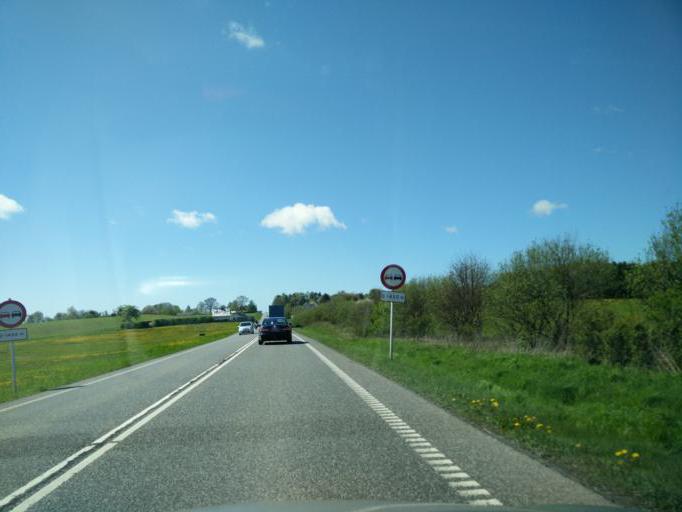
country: DK
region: Capital Region
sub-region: Gribskov Kommune
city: Helsinge
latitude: 56.0071
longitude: 12.2330
